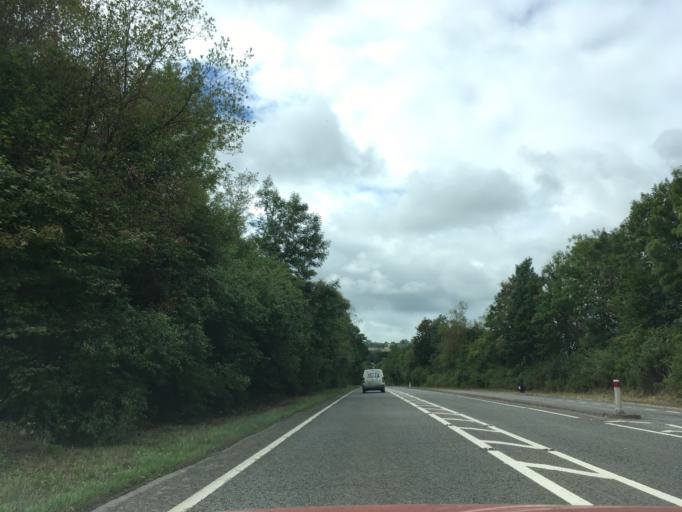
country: GB
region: Wales
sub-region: Carmarthenshire
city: Llandeilo
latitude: 51.8920
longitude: -4.0191
